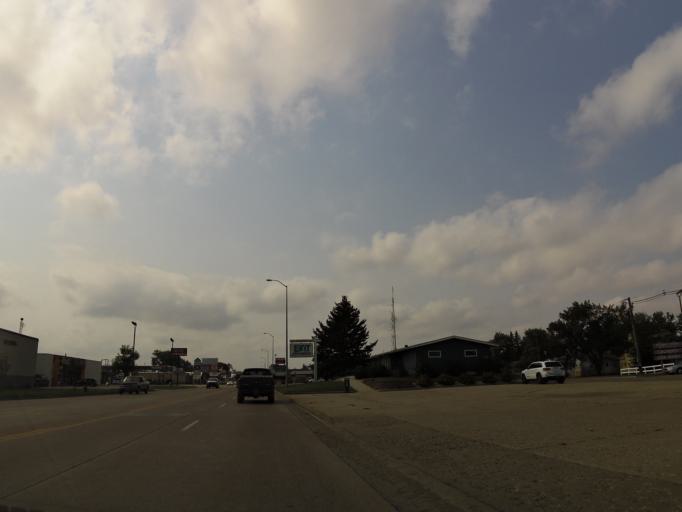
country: US
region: South Dakota
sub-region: Codington County
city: Watertown
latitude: 44.8901
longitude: -97.1008
